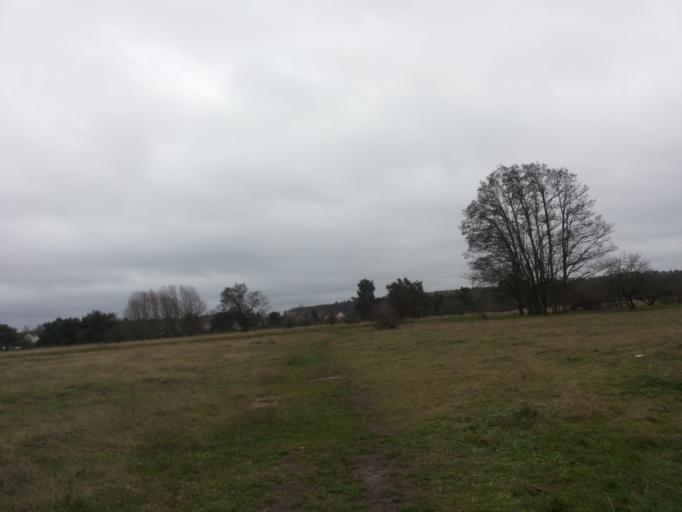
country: DE
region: Bavaria
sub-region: Regierungsbezirk Mittelfranken
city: Wendelstein
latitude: 49.4028
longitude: 11.1678
